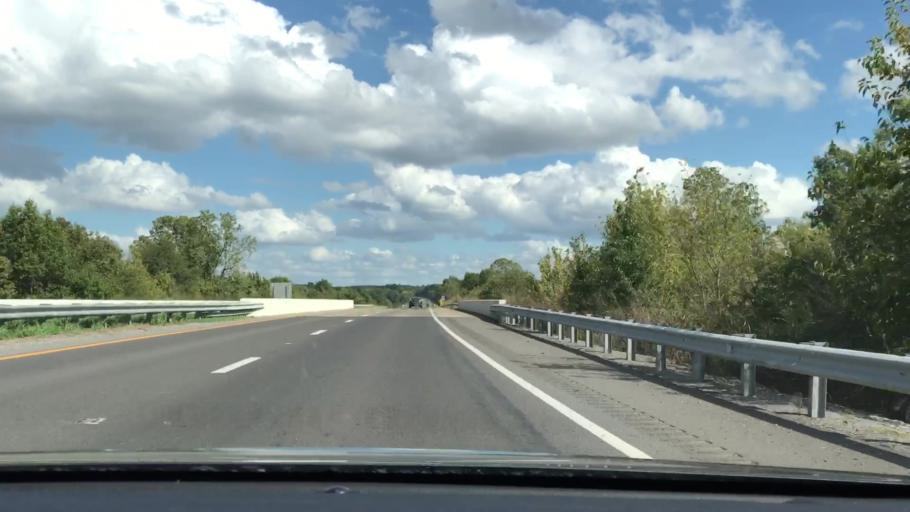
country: US
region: Kentucky
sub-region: Graves County
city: Mayfield
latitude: 36.7690
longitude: -88.6383
